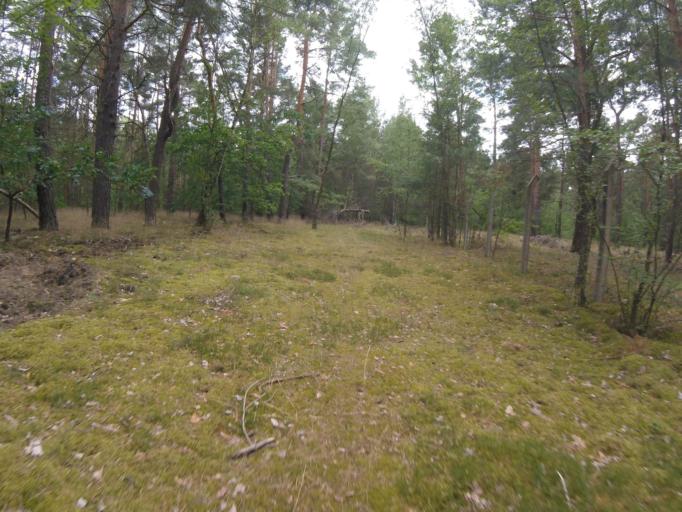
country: DE
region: Brandenburg
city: Wildau
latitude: 52.3300
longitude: 13.6664
